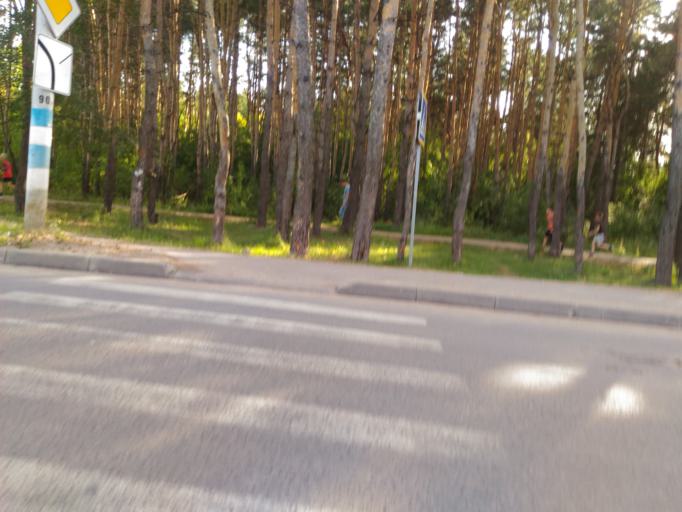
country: RU
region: Ulyanovsk
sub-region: Ulyanovskiy Rayon
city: Ulyanovsk
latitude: 54.3528
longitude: 48.5259
